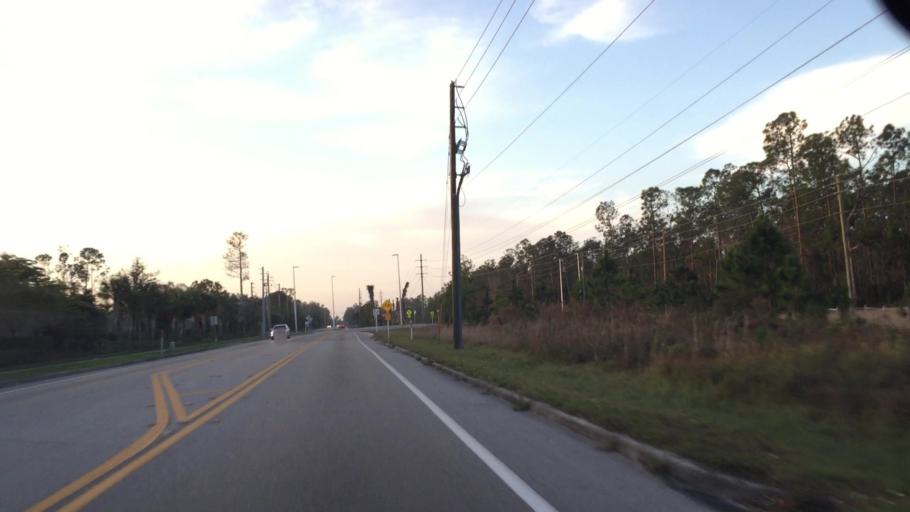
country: US
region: Florida
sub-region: Lee County
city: Villas
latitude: 26.5664
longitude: -81.8471
